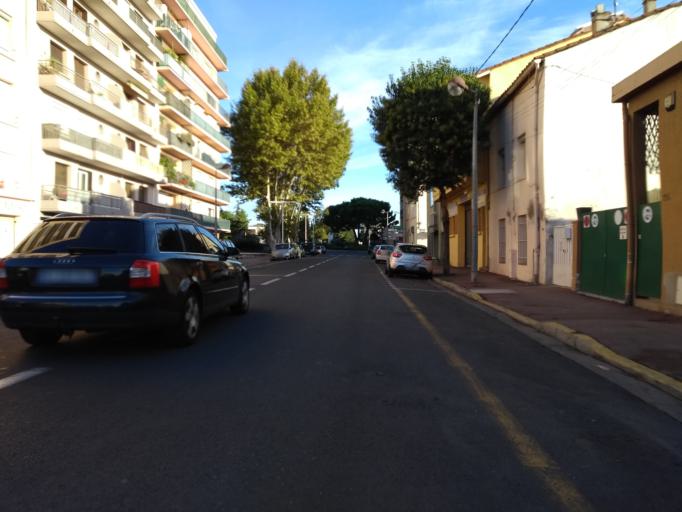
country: FR
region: Languedoc-Roussillon
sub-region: Departement des Pyrenees-Orientales
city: Perpignan
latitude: 42.7147
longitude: 2.8886
